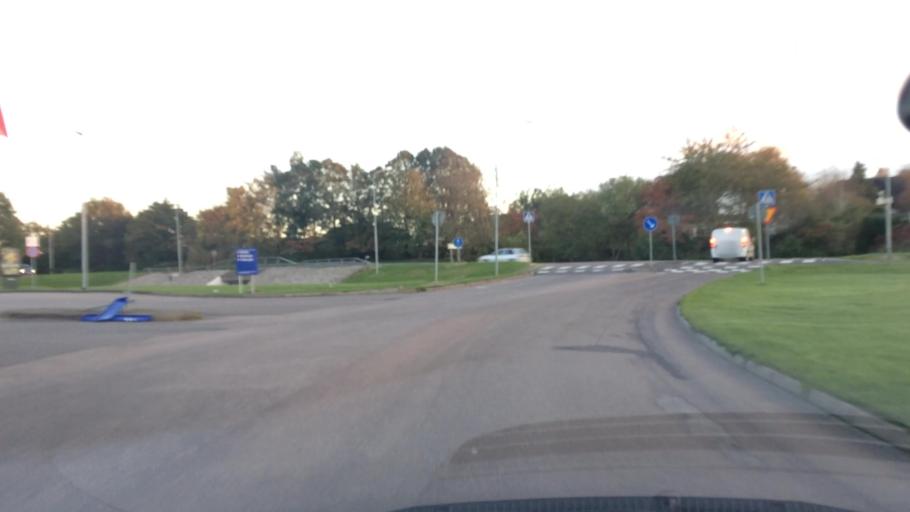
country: SE
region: Halland
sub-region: Kungsbacka Kommun
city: Kungsbacka
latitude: 57.5061
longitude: 12.0631
